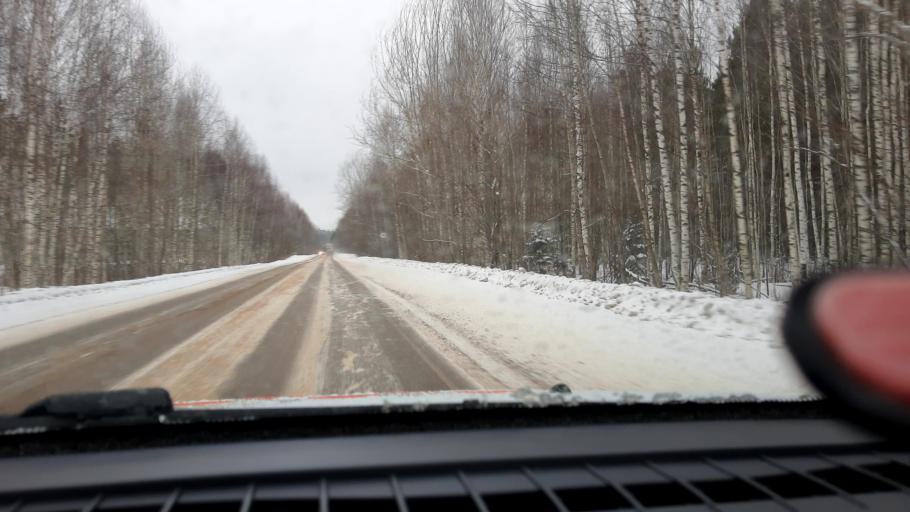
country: RU
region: Nizjnij Novgorod
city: Pamyat' Parizhskoy Kommuny
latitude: 56.2748
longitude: 44.4009
